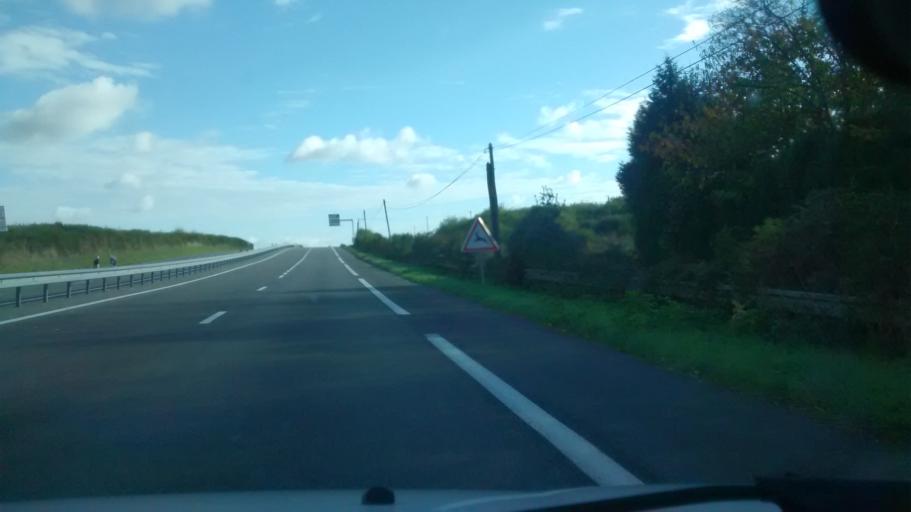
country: FR
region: Pays de la Loire
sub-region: Departement de Maine-et-Loire
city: Pouance
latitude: 47.7310
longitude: -1.1157
